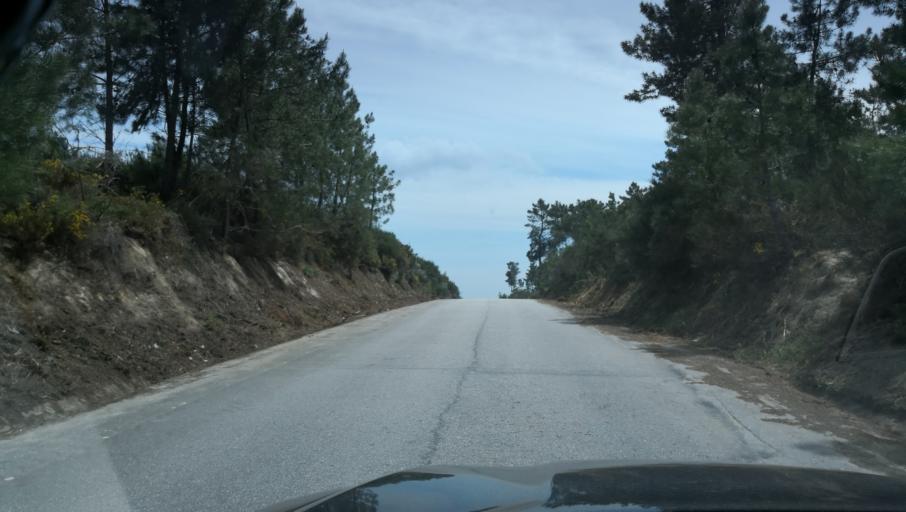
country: PT
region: Vila Real
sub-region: Vila Real
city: Vila Real
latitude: 41.2809
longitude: -7.8030
